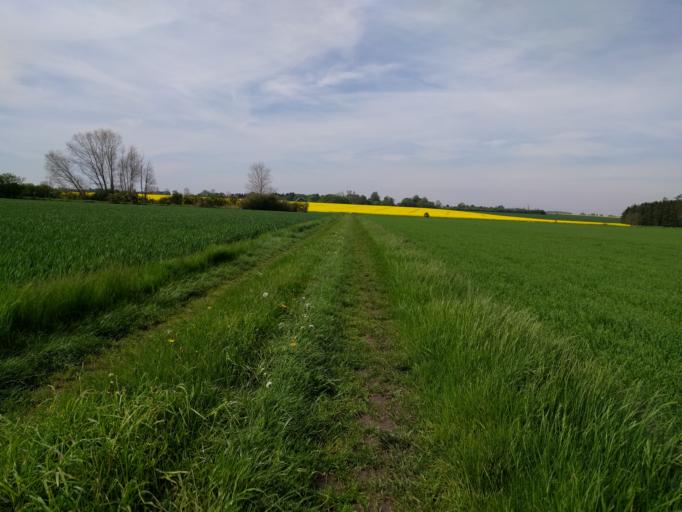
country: DK
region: South Denmark
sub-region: Odense Kommune
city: Bullerup
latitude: 55.4000
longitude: 10.5294
